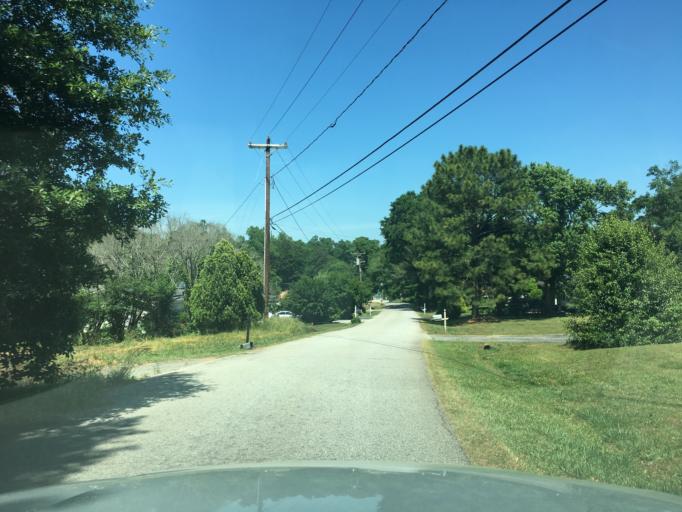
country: US
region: South Carolina
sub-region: Spartanburg County
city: Wellford
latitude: 34.9298
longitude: -82.1123
